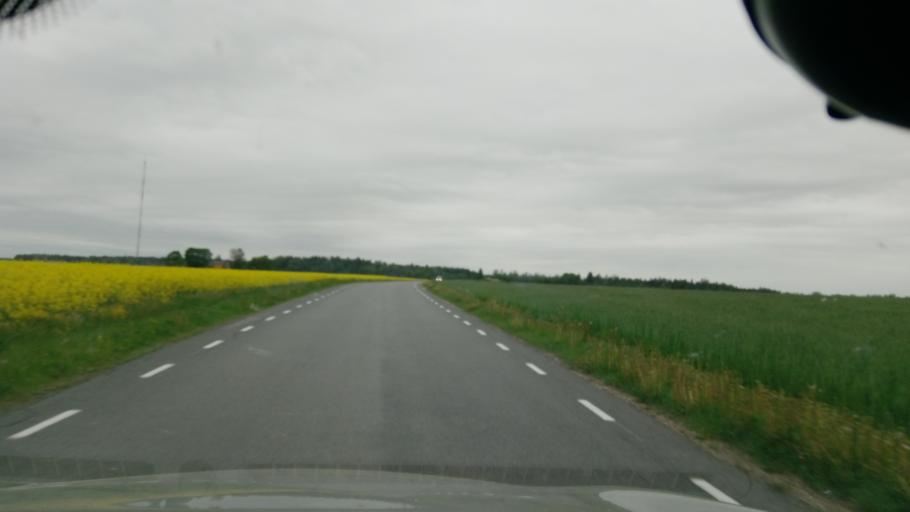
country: EE
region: Jaervamaa
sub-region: Koeru vald
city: Koeru
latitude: 58.9961
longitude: 26.0637
